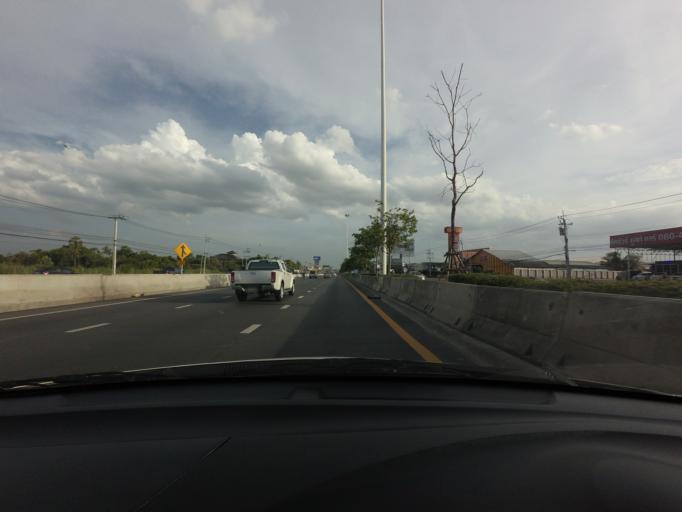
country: TH
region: Nonthaburi
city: Bang Bua Thong
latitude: 13.9233
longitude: 100.4526
